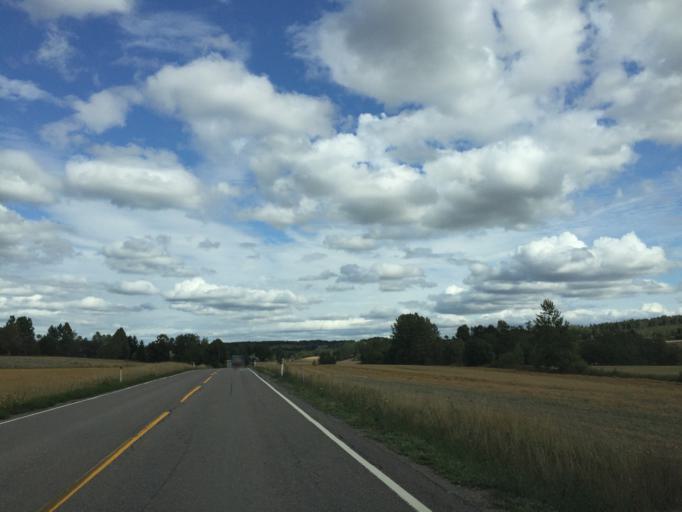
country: NO
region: Ostfold
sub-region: Hobol
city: Elvestad
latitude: 59.6166
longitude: 10.9383
